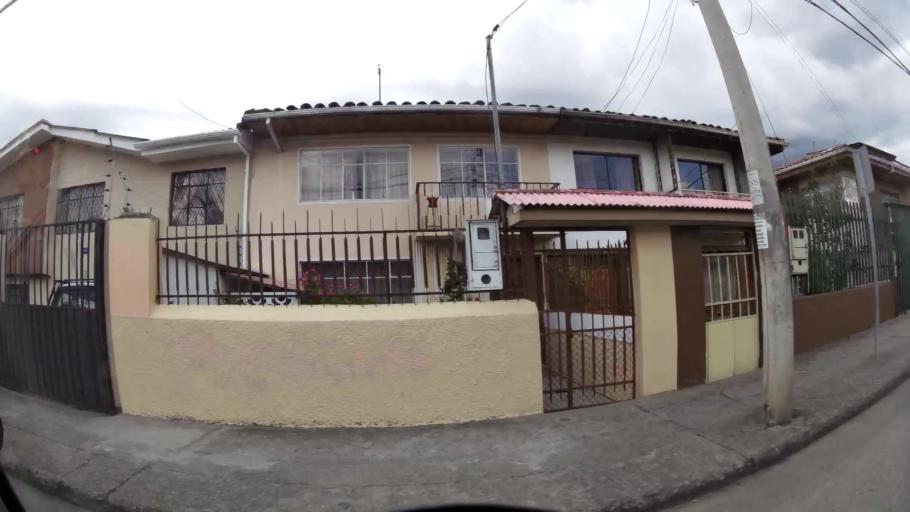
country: EC
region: Azuay
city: Cuenca
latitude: -2.8880
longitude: -79.0066
